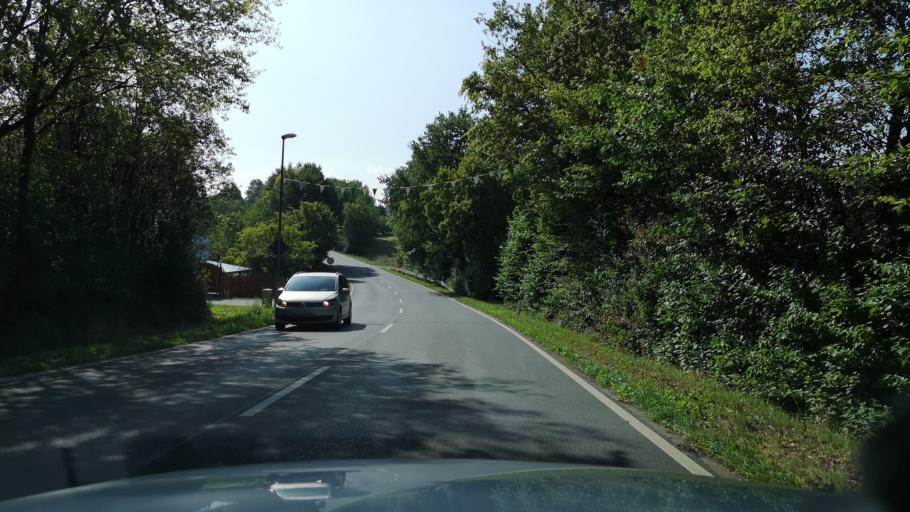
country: DE
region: North Rhine-Westphalia
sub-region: Regierungsbezirk Arnsberg
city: Frondenberg
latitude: 51.4950
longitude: 7.7740
